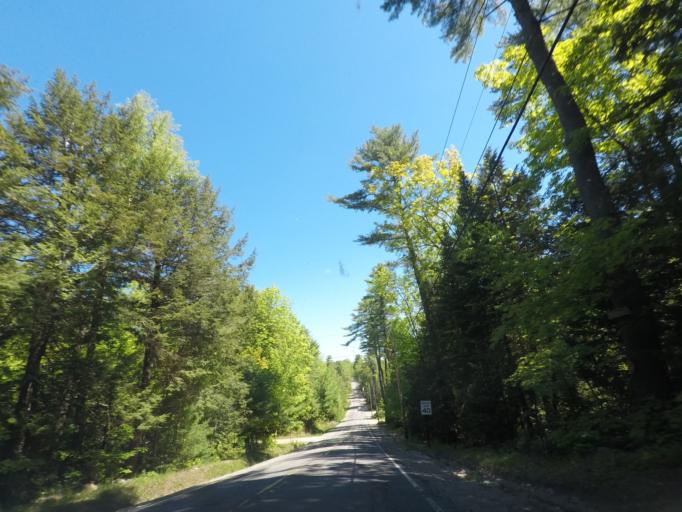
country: US
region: Maine
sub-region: Kennebec County
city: Manchester
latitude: 44.2671
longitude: -69.9018
